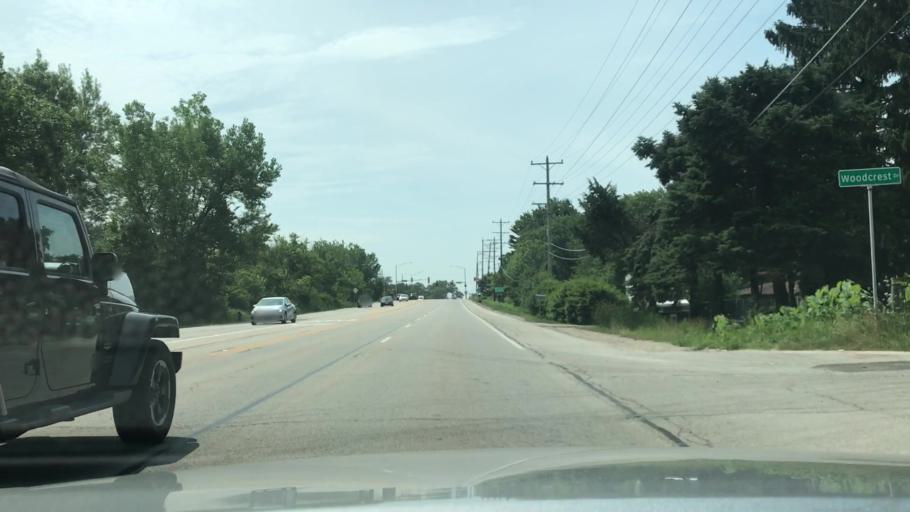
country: US
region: Illinois
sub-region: DuPage County
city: Darien
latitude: 41.7260
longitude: -88.0098
